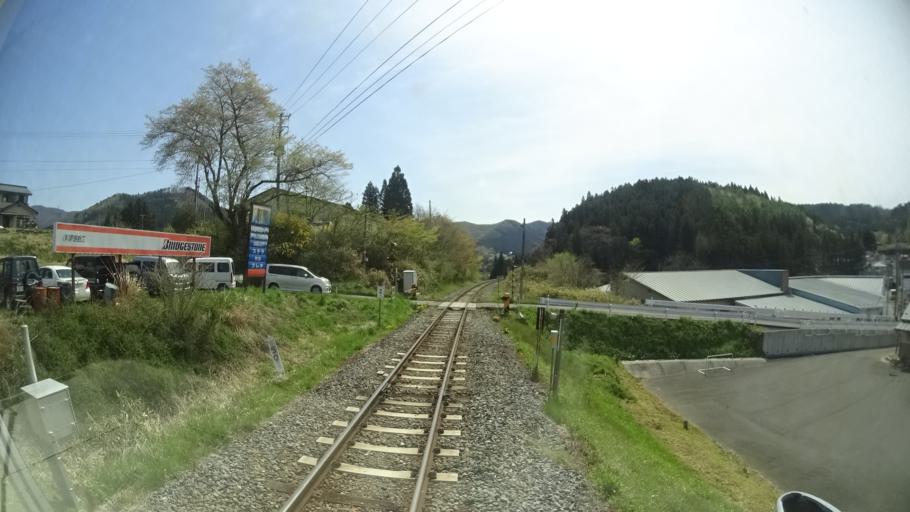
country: JP
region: Iwate
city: Ofunato
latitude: 38.9394
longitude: 141.4559
